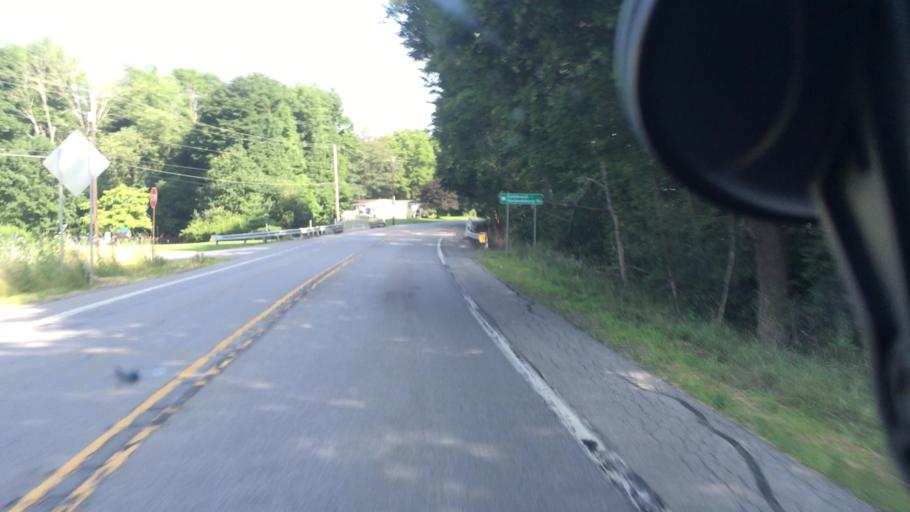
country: US
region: Pennsylvania
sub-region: Butler County
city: Slippery Rock
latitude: 41.0272
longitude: -80.1901
